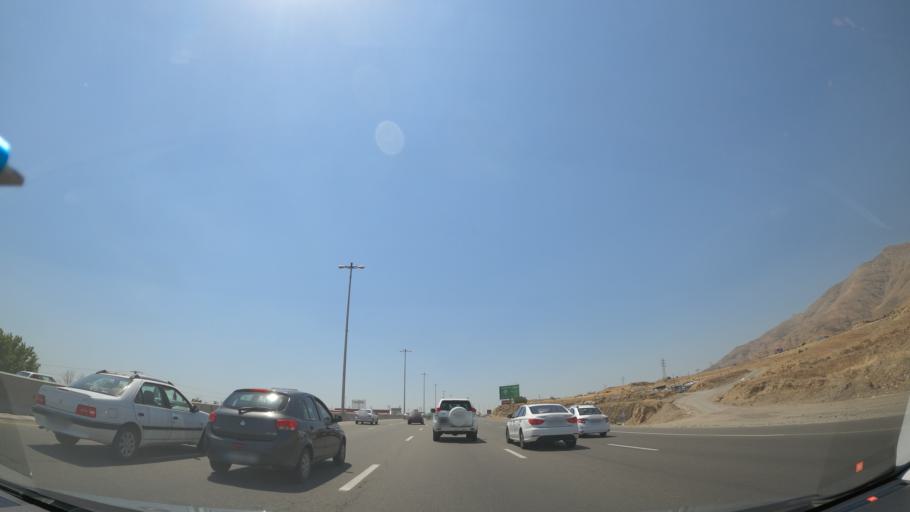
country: IR
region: Tehran
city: Shahr-e Qods
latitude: 35.7453
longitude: 51.0915
